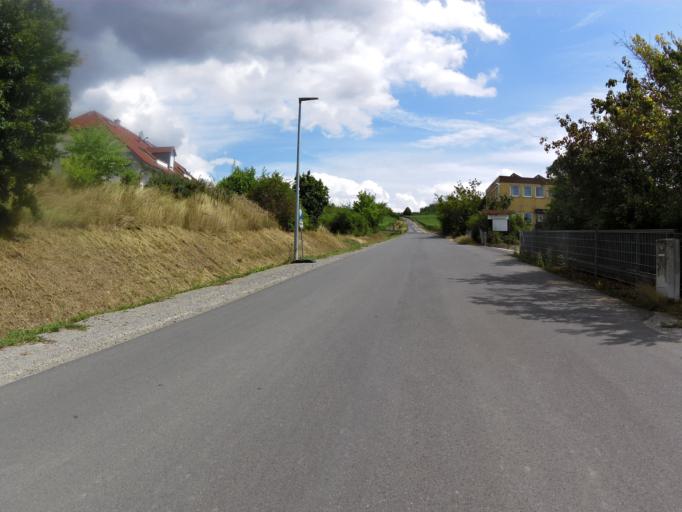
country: DE
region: Bavaria
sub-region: Regierungsbezirk Unterfranken
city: Sommerhausen
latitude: 49.6970
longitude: 10.0288
